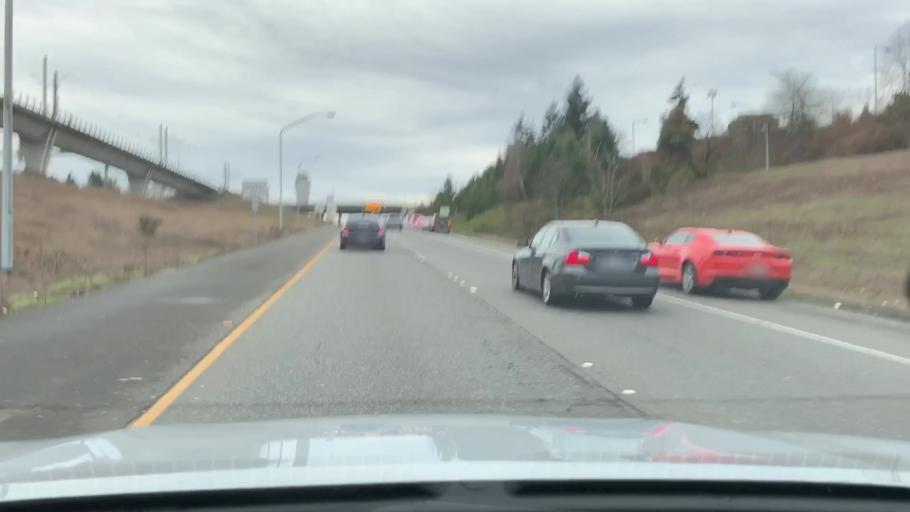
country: US
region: Washington
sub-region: King County
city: SeaTac
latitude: 47.4624
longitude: -122.2953
